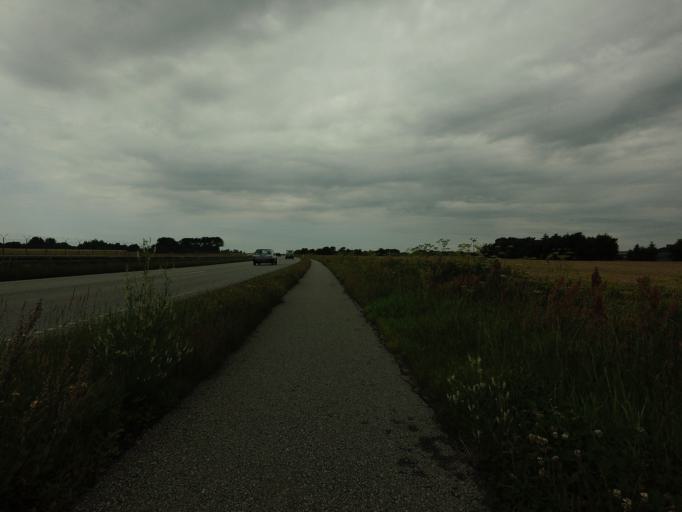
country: DK
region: North Denmark
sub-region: Alborg Kommune
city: Vadum
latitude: 57.1053
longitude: 9.8812
